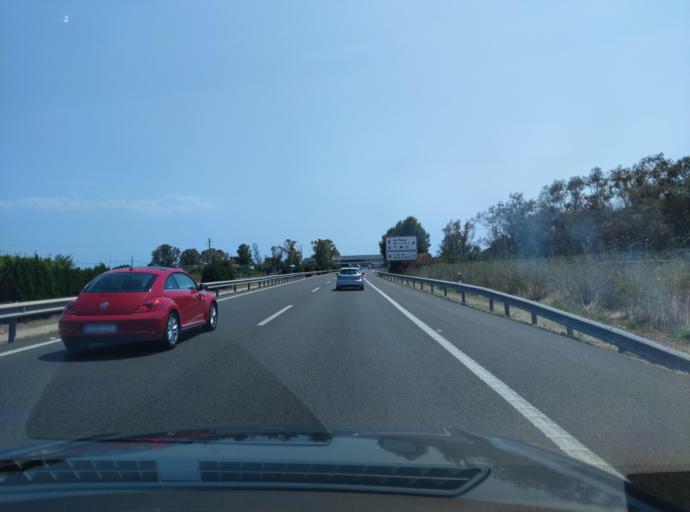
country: ES
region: Valencia
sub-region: Provincia de Castello
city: Alquerias del Nino Perdido
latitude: 39.8690
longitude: -0.1223
